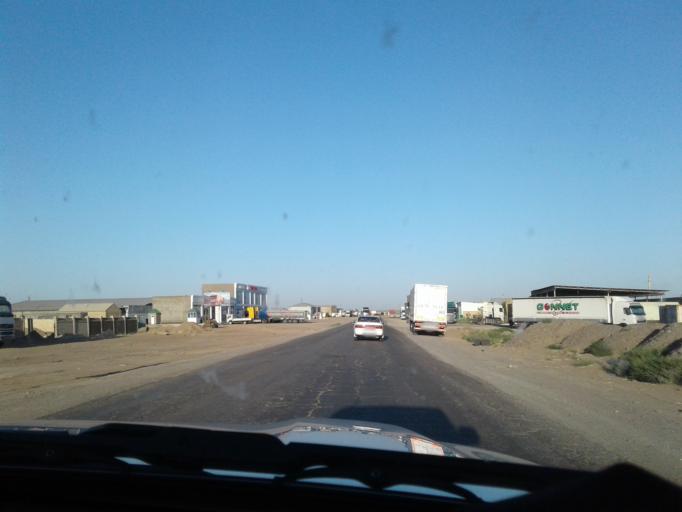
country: TM
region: Mary
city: Mary
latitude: 37.5660
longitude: 61.8144
